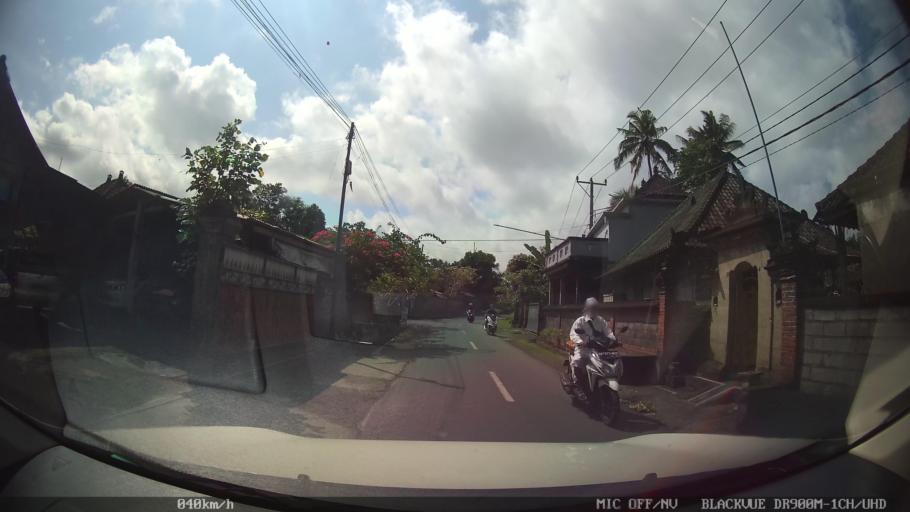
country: ID
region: Bali
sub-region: Kabupaten Gianyar
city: Ubud
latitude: -8.5234
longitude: 115.2988
